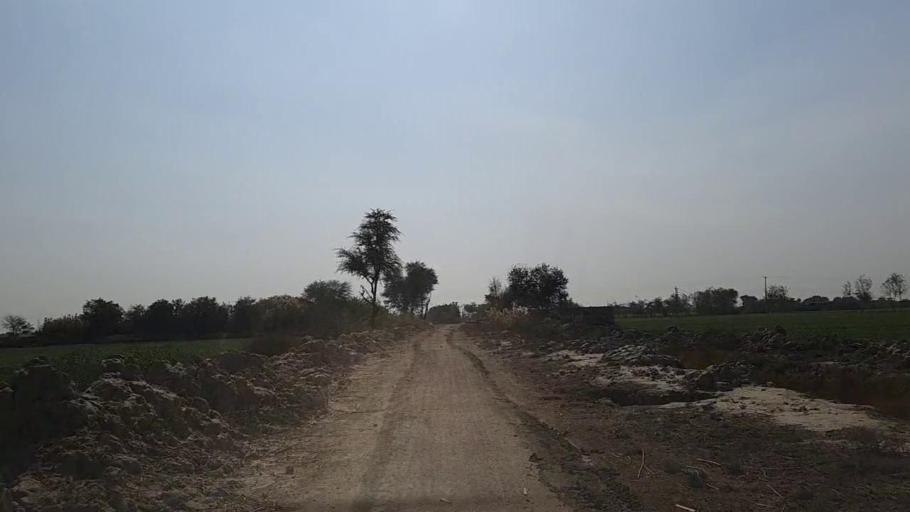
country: PK
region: Sindh
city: Nawabshah
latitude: 26.2888
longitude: 68.4805
